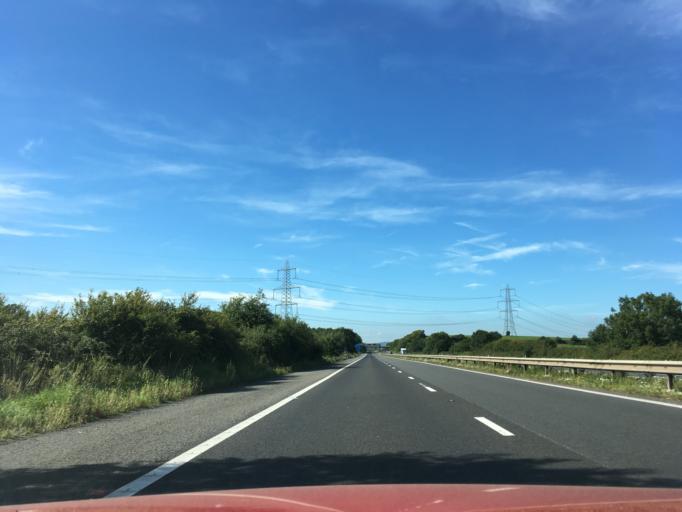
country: GB
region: England
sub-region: South Gloucestershire
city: Almondsbury
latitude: 51.5825
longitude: -2.5935
